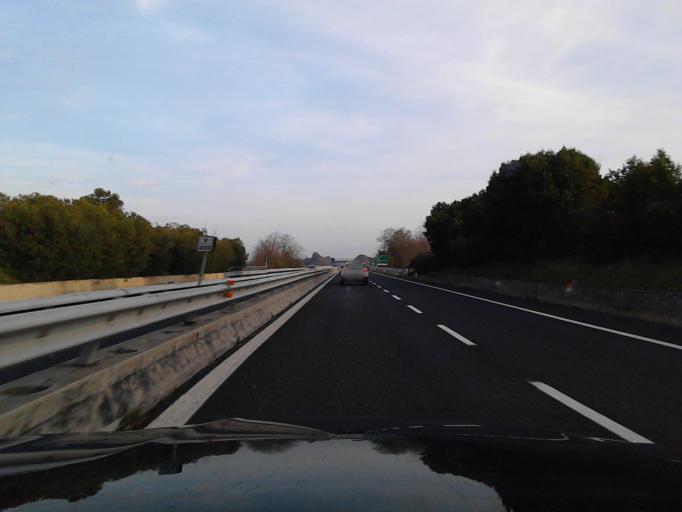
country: IT
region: Abruzzo
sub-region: Provincia di Chieti
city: Ortona
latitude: 42.3355
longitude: 14.3674
